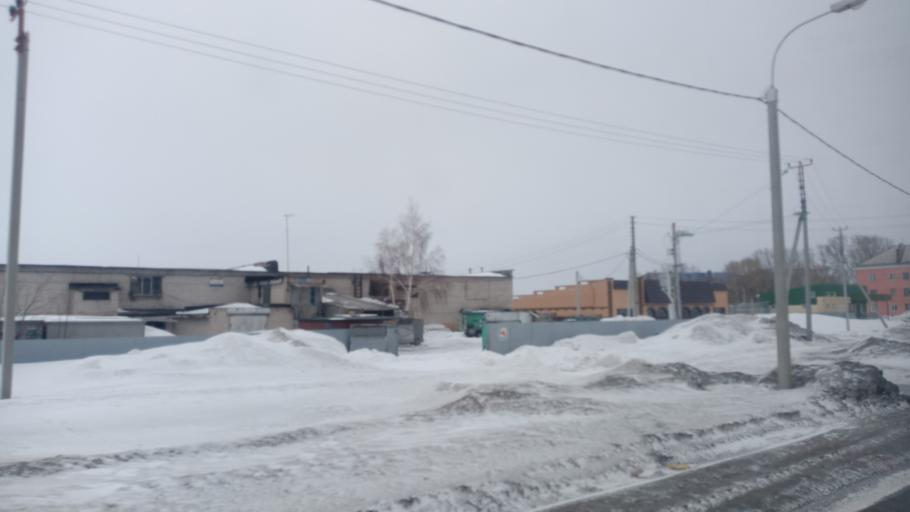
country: RU
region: Altai Krai
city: Novosilikatnyy
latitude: 53.3888
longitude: 83.6622
